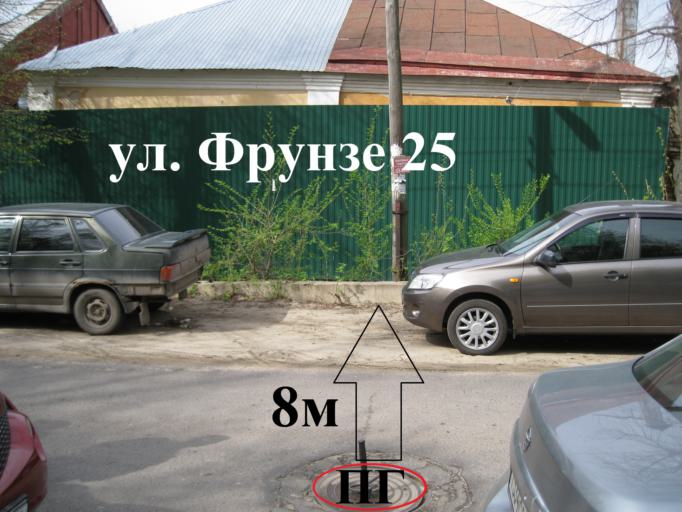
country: RU
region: Voronezj
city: Voronezh
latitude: 51.6561
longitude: 39.2043
